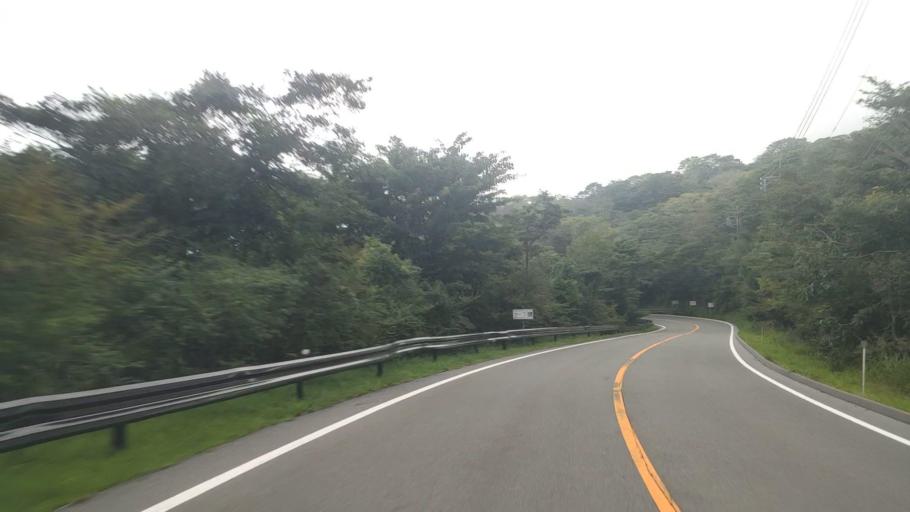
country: JP
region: Shizuoka
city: Fuji
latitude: 35.2866
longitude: 138.7783
